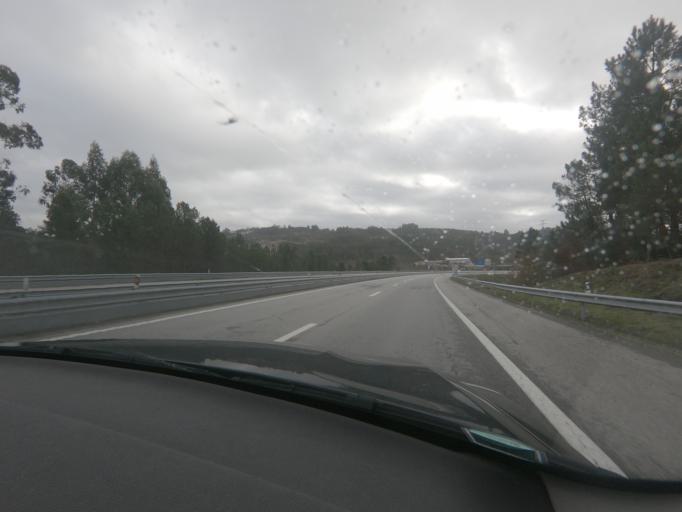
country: PT
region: Viseu
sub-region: Castro Daire
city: Castro Daire
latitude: 40.8270
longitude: -7.9353
